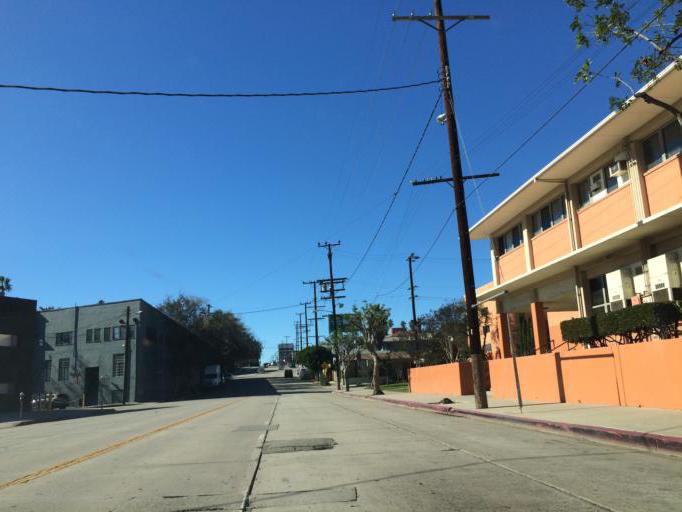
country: US
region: California
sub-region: Los Angeles County
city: Silver Lake
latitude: 34.0958
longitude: -118.2811
